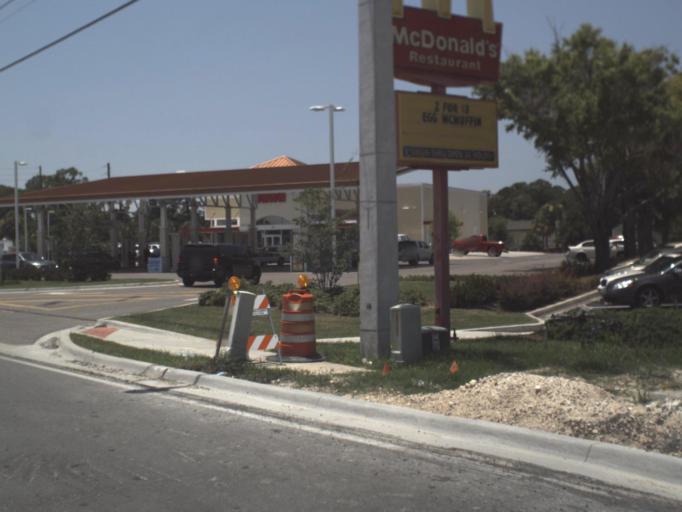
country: US
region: Florida
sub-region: Pasco County
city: Port Richey
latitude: 28.2814
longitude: -82.7169
